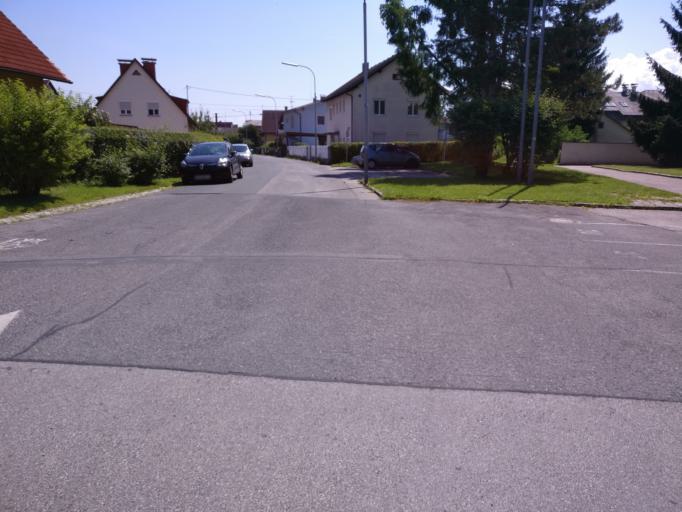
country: AT
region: Carinthia
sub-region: Klagenfurt am Woerthersee
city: Klagenfurt am Woerthersee
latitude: 46.6102
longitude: 14.2842
